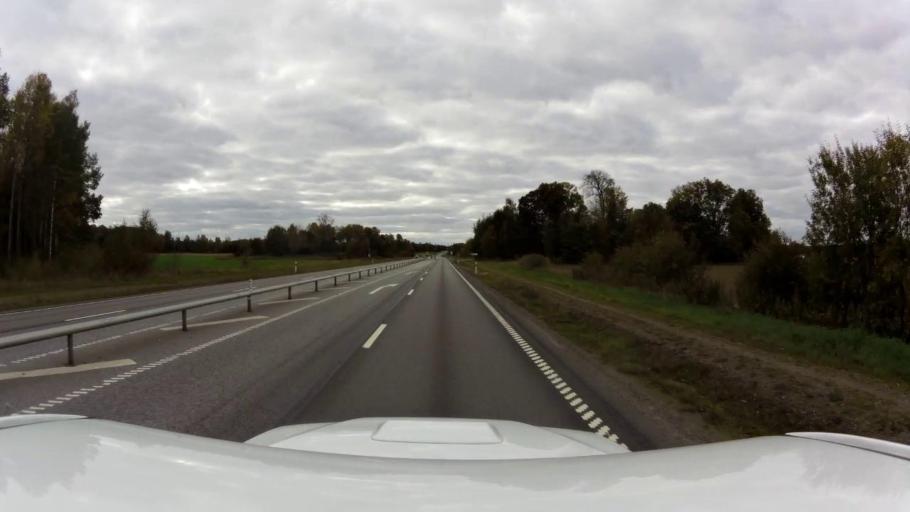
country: SE
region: OEstergoetland
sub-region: Linkopings Kommun
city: Malmslatt
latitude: 58.3727
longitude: 15.5434
